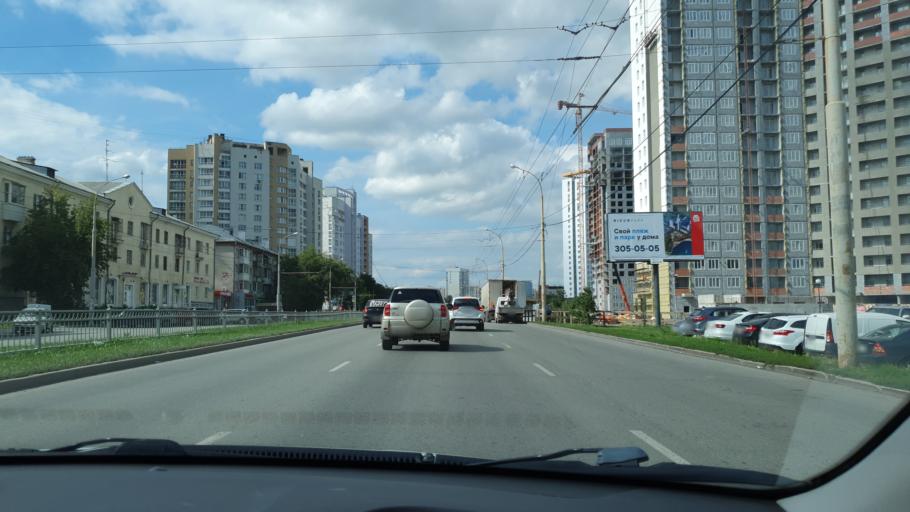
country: RU
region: Sverdlovsk
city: Yekaterinburg
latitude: 56.7828
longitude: 60.6540
